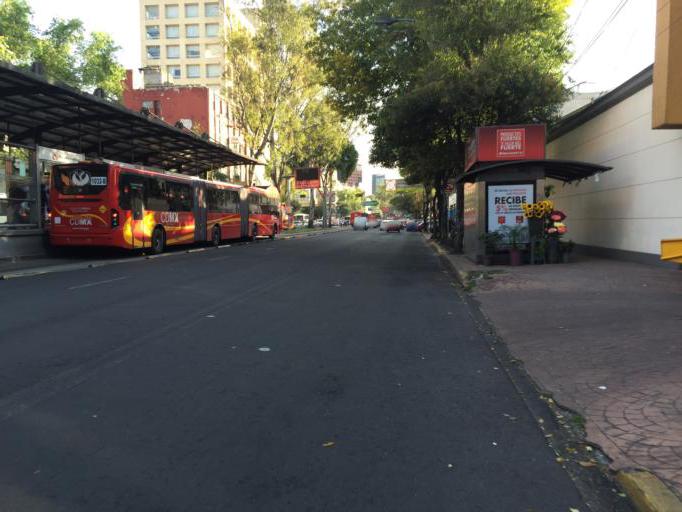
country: MX
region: Mexico City
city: Cuauhtemoc
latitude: 19.4363
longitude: -99.1573
